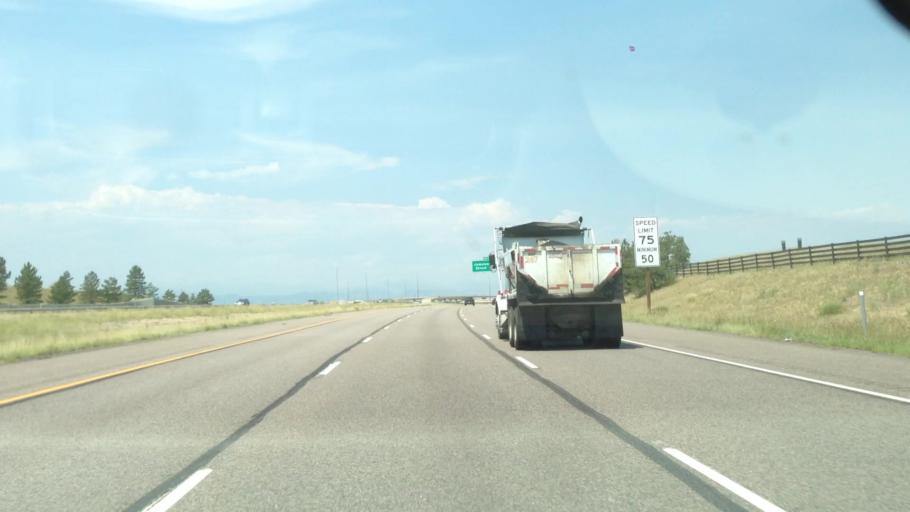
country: US
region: Colorado
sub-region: Douglas County
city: Meridian
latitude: 39.5514
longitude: -104.8538
